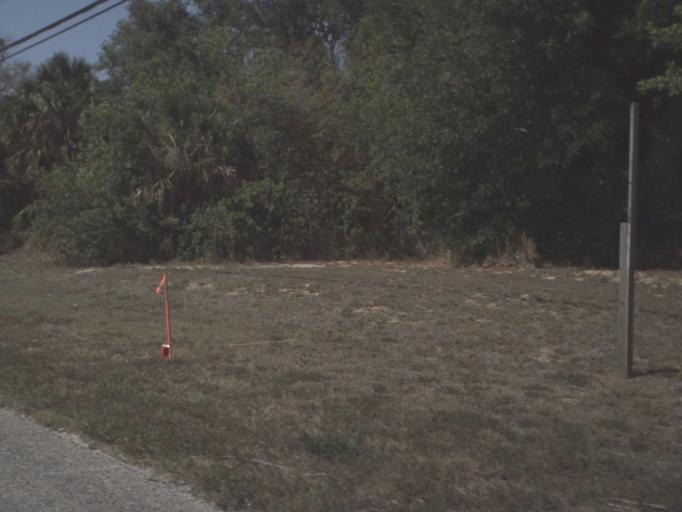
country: US
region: Florida
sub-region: Brevard County
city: Rockledge
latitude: 28.3023
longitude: -80.7036
